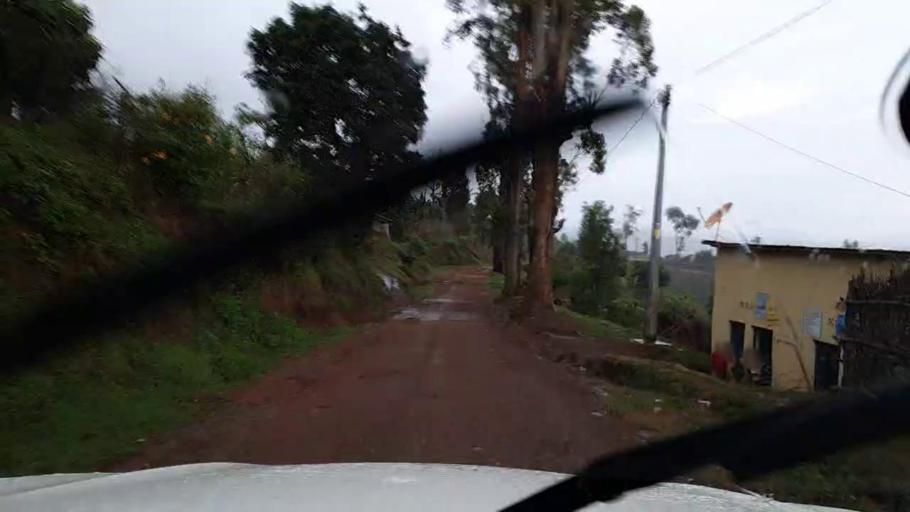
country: BI
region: Kayanza
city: Kayanza
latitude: -2.7793
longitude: 29.5354
